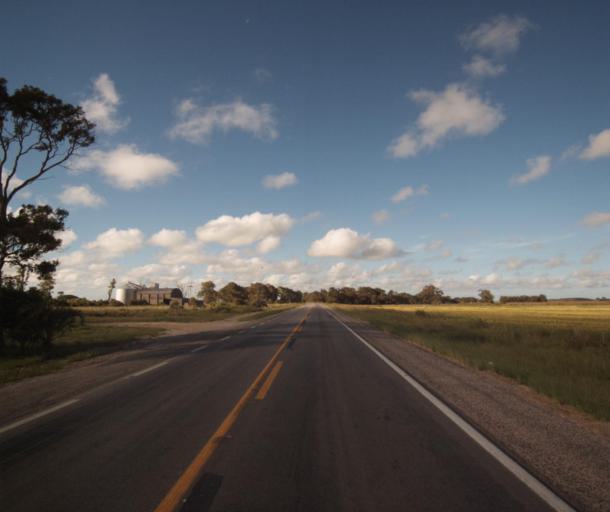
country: BR
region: Rio Grande do Sul
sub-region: Arroio Grande
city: Arroio Grande
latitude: -32.8515
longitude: -52.7026
